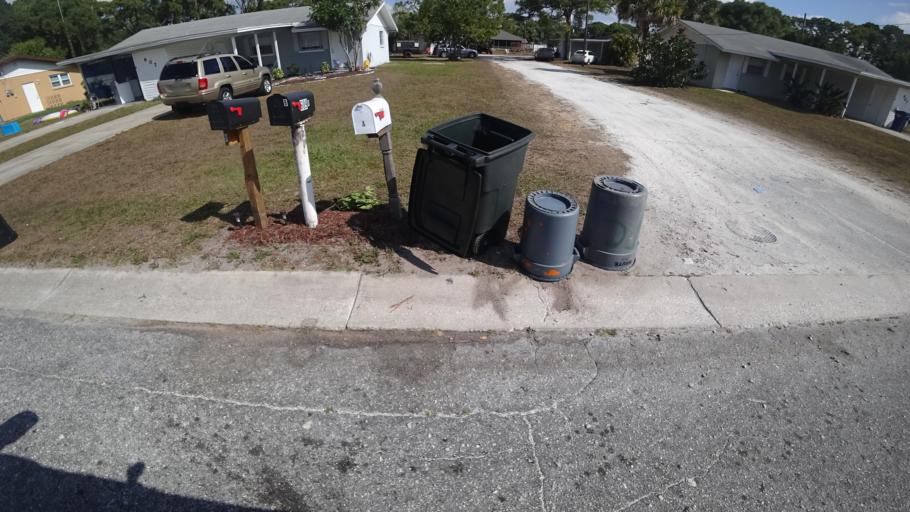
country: US
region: Florida
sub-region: Manatee County
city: Whitfield
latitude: 27.4225
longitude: -82.5689
